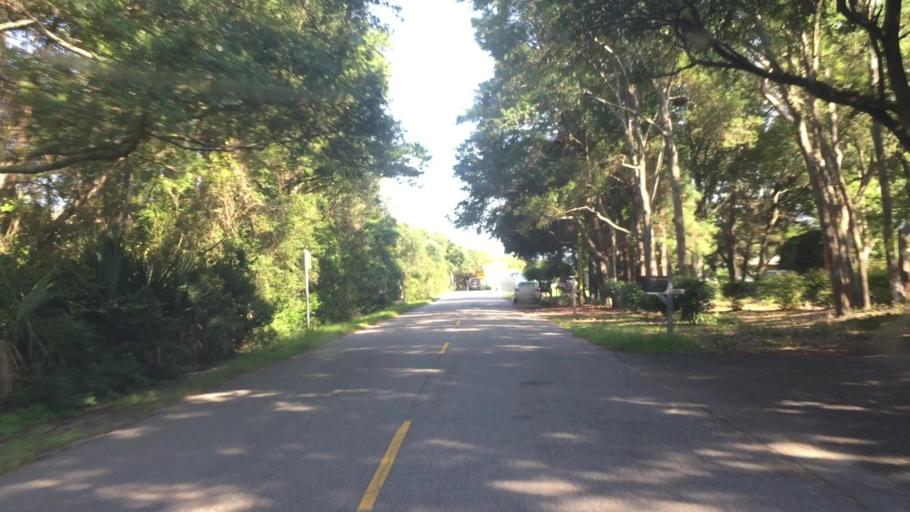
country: US
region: South Carolina
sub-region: Horry County
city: Myrtle Beach
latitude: 33.7481
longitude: -78.8096
